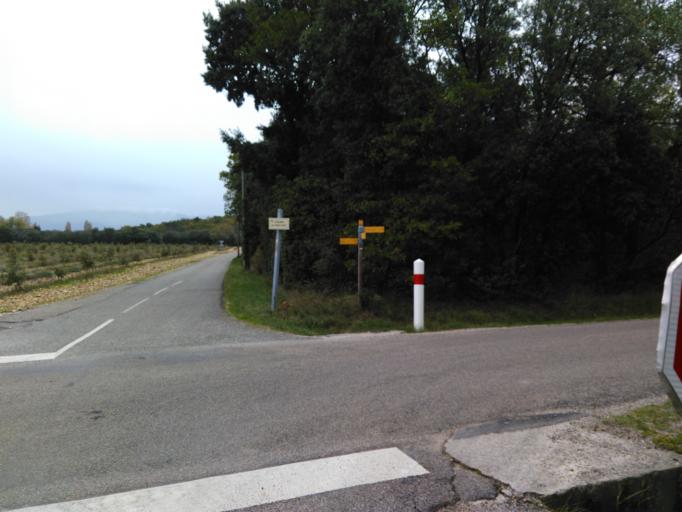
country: FR
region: Provence-Alpes-Cote d'Azur
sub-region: Departement du Vaucluse
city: Grillon
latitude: 44.3697
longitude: 4.9069
